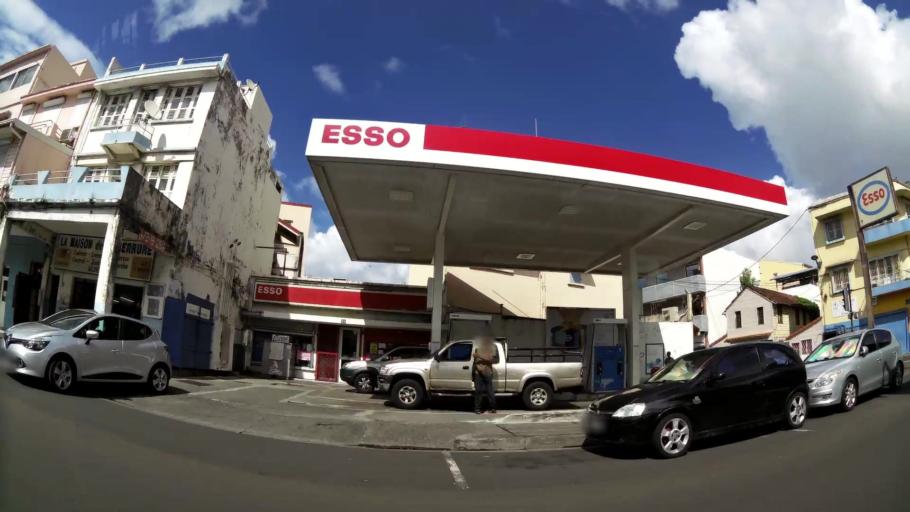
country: MQ
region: Martinique
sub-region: Martinique
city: Fort-de-France
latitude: 14.6077
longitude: -61.0699
